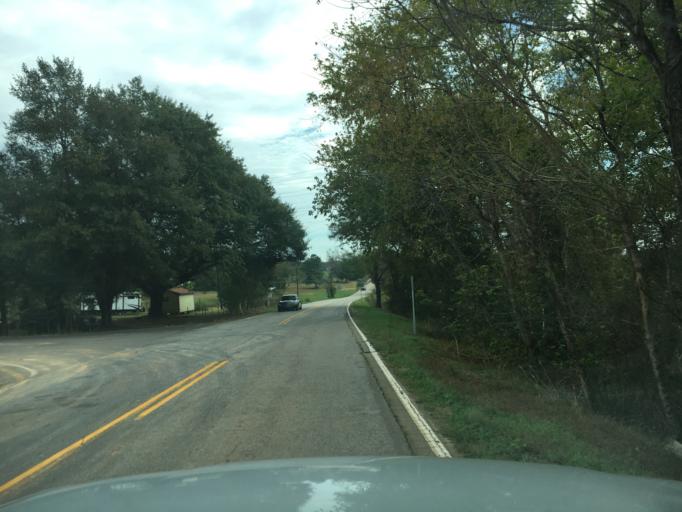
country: US
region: South Carolina
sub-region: Spartanburg County
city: Duncan
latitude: 34.9367
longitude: -82.1790
